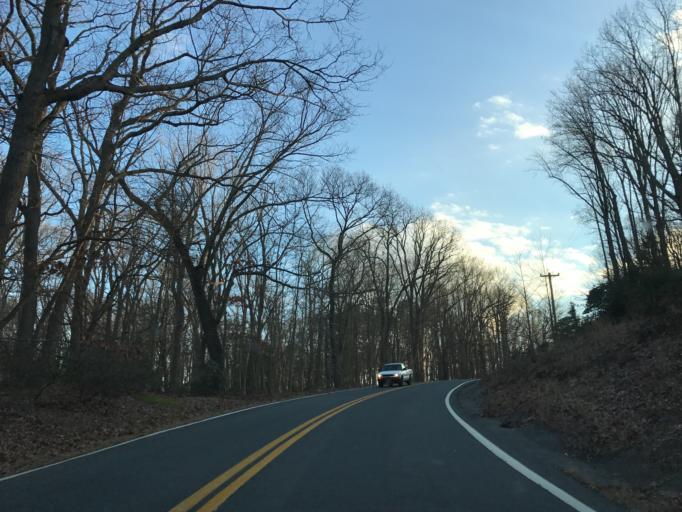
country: US
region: Maryland
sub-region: Cecil County
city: Charlestown
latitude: 39.4857
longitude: -75.9814
